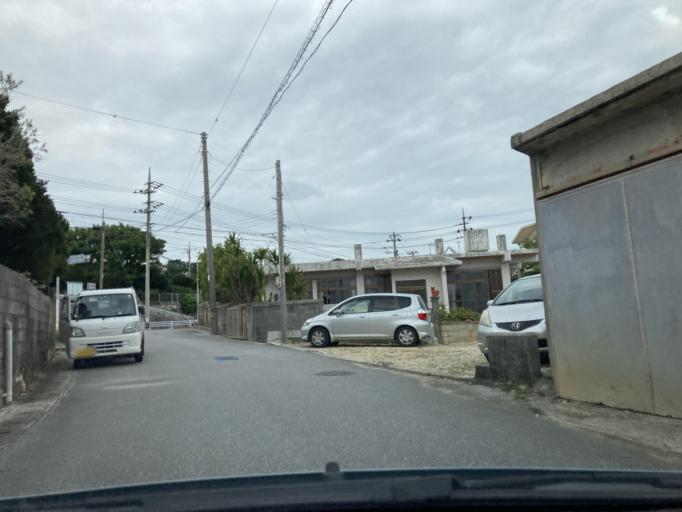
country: JP
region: Okinawa
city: Tomigusuku
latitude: 26.1407
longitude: 127.7918
